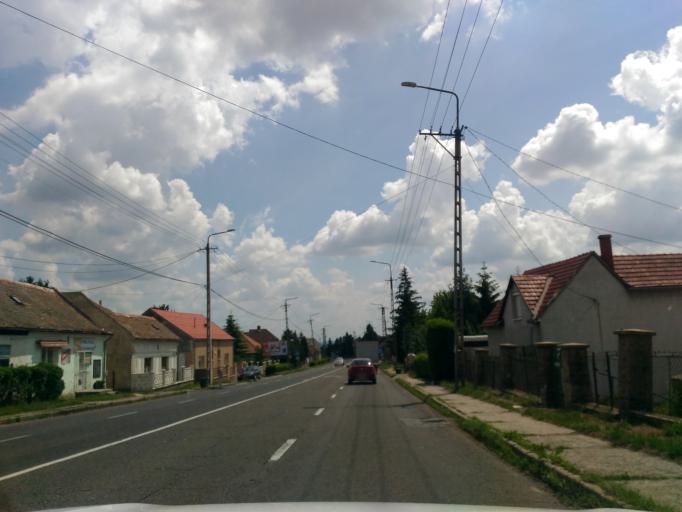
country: HU
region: Baranya
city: Pecs
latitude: 46.1133
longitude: 18.2619
